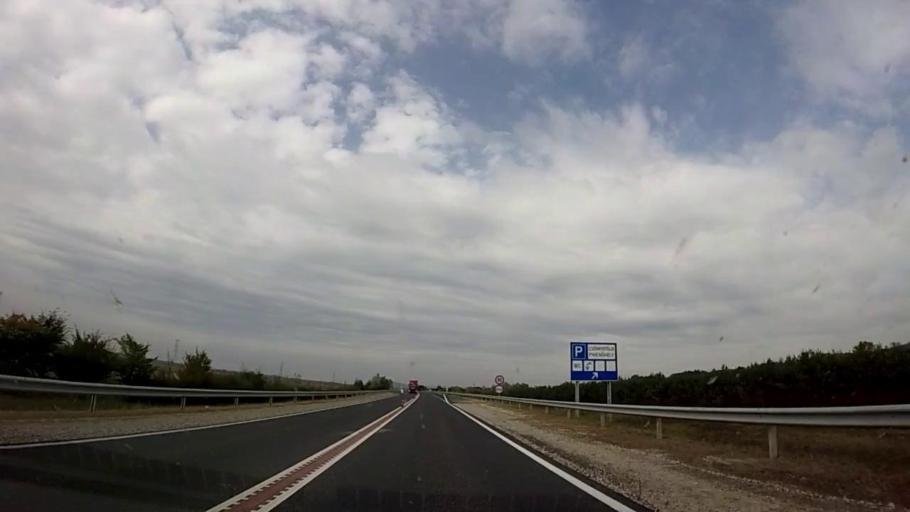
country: HR
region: Medimurska
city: Domasinec
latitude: 46.5007
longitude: 16.6161
